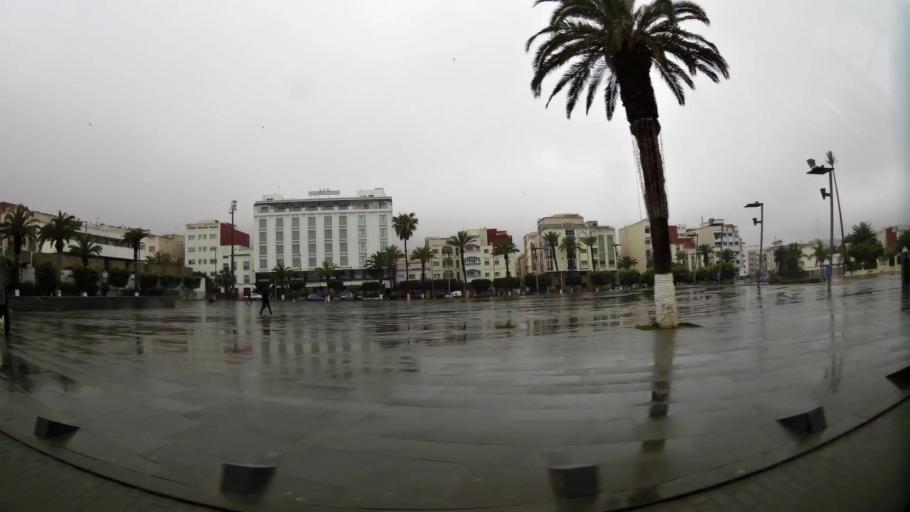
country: MA
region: Taza-Al Hoceima-Taounate
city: Al Hoceima
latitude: 35.2449
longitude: -3.9293
